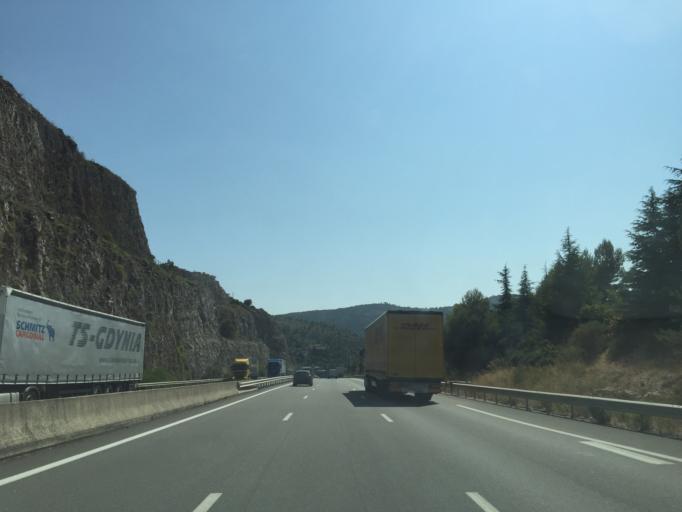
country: FR
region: Provence-Alpes-Cote d'Azur
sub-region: Departement des Alpes-Maritimes
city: La Turbie
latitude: 43.7520
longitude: 7.3934
